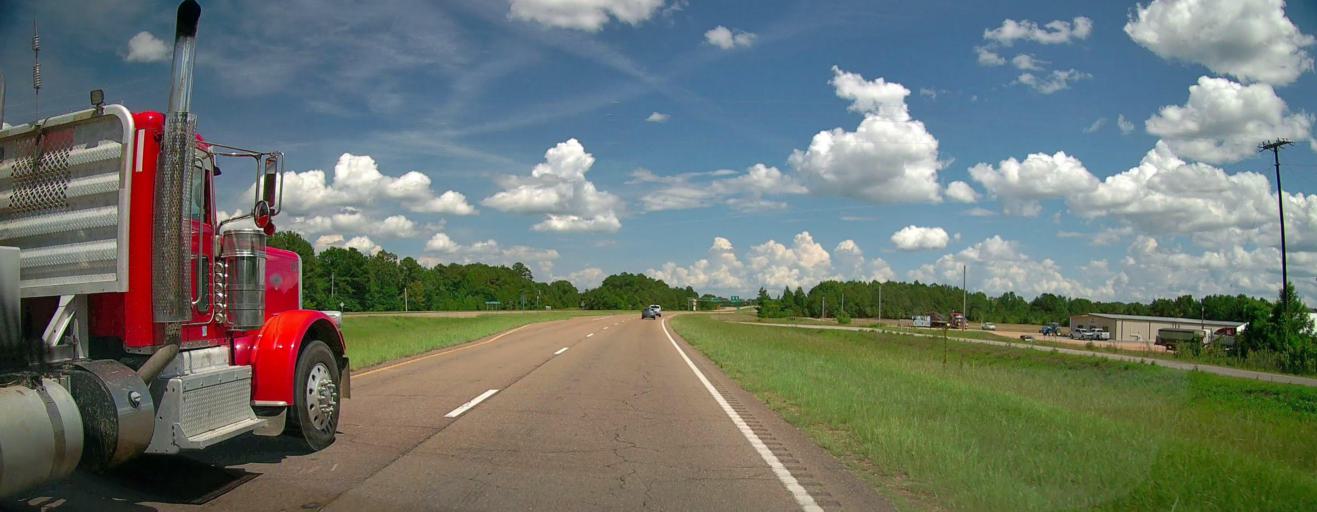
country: US
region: Mississippi
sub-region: Monroe County
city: Aberdeen
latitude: 33.8174
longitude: -88.5002
